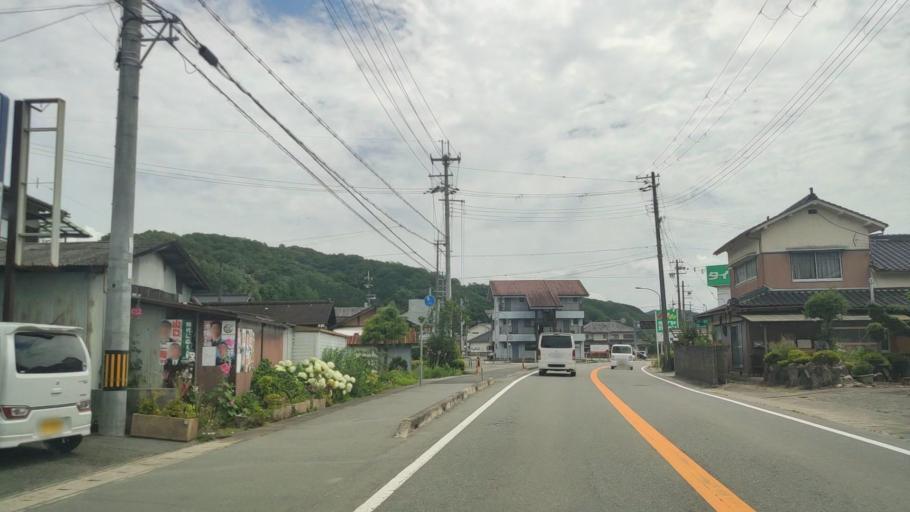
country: JP
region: Hyogo
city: Yamazakicho-nakabirose
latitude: 35.0190
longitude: 134.3711
